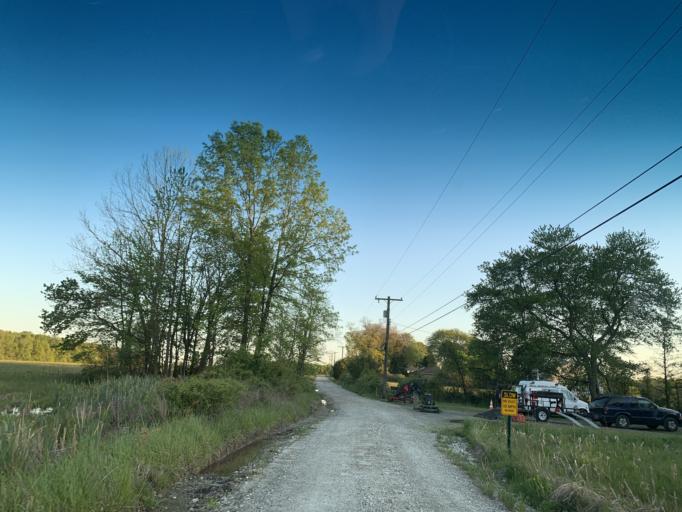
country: US
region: Maryland
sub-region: Harford County
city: Aberdeen
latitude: 39.5090
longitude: -76.1903
